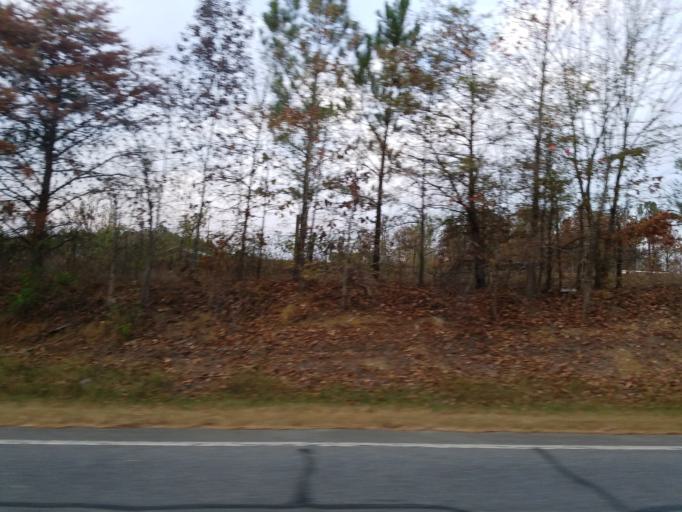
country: US
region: Georgia
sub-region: Murray County
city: Chatsworth
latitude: 34.6049
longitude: -84.8166
